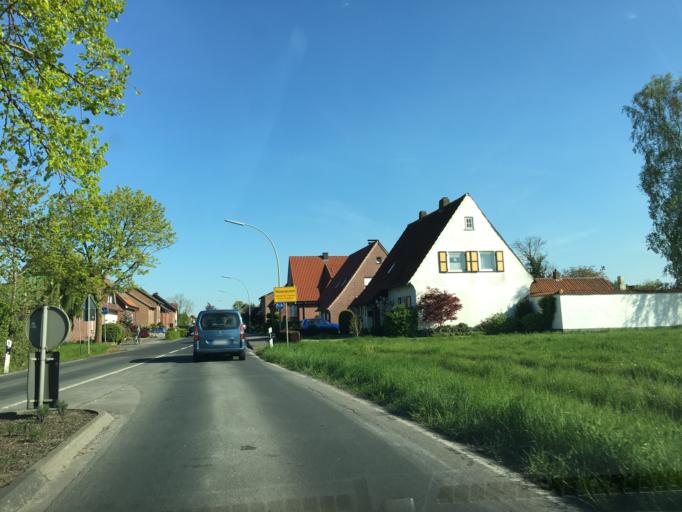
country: DE
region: North Rhine-Westphalia
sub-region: Regierungsbezirk Munster
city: Senden
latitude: 51.8260
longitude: 7.5303
